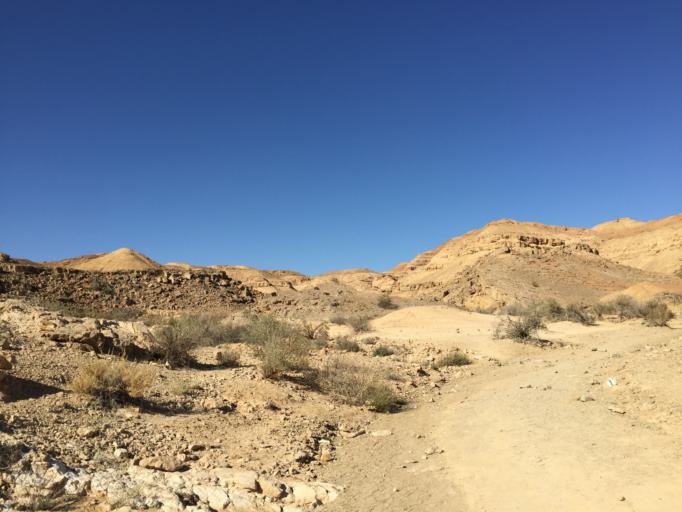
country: IL
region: Southern District
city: Mitzpe Ramon
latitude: 30.6025
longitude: 34.9492
